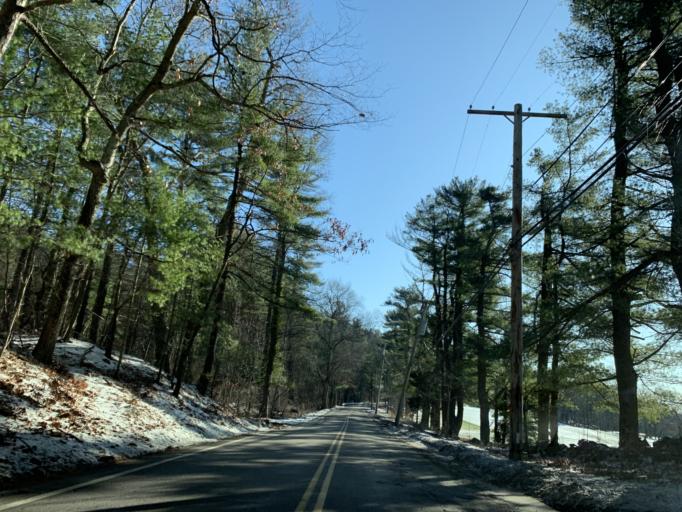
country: US
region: Massachusetts
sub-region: Norfolk County
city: Canton
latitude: 42.2001
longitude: -71.1287
